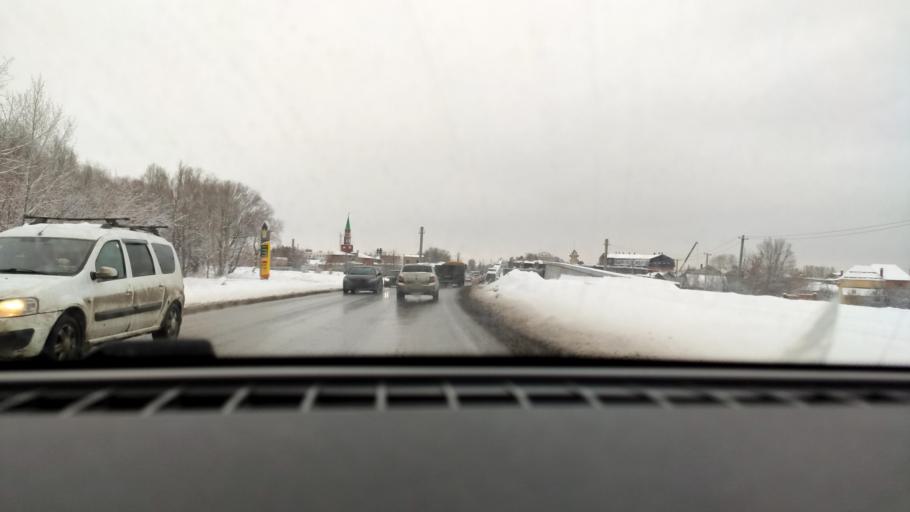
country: RU
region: Samara
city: Samara
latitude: 53.1387
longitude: 50.1019
